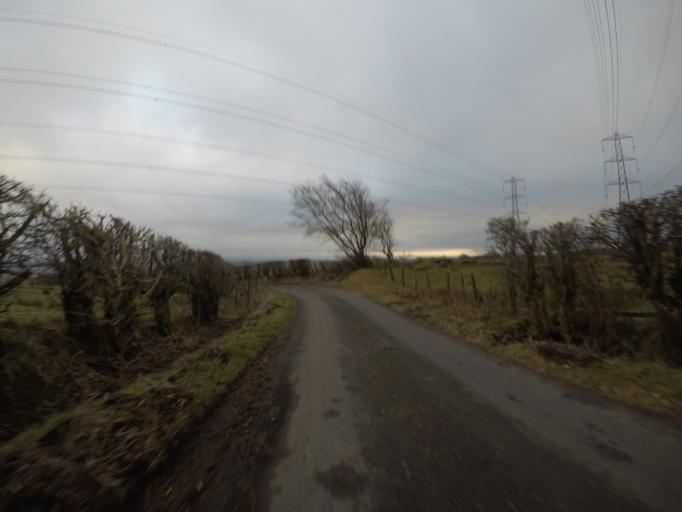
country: GB
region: Scotland
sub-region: North Ayrshire
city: Dalry
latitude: 55.7228
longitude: -4.7625
